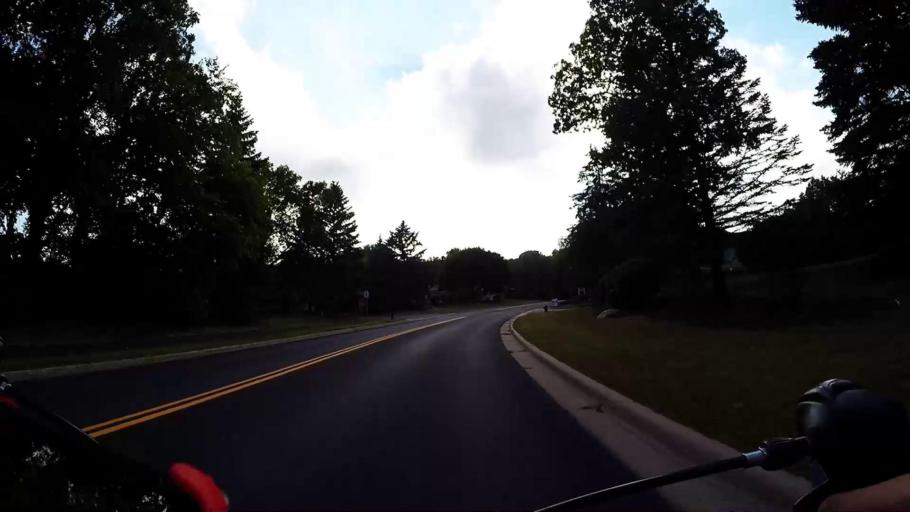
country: US
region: Minnesota
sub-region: Hennepin County
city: Eden Prairie
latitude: 44.8859
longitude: -93.4504
